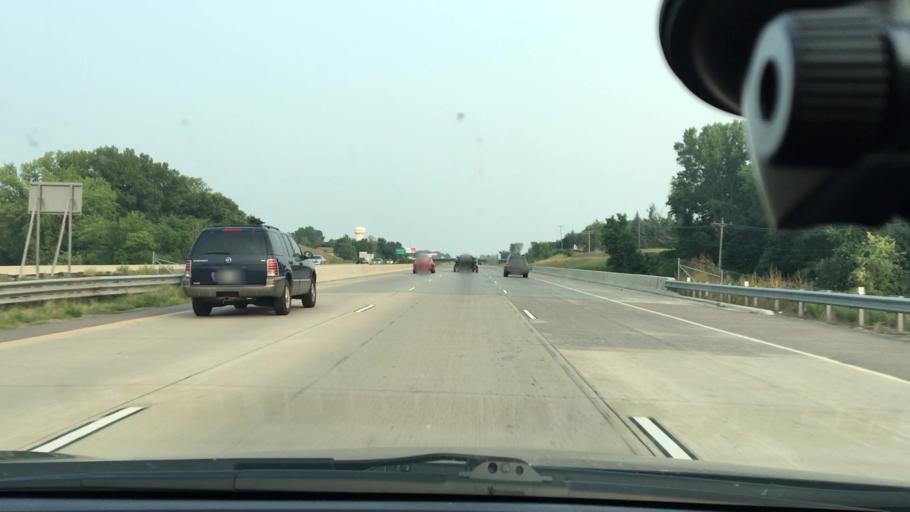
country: US
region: Minnesota
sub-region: Hennepin County
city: Rogers
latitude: 45.2150
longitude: -93.5912
